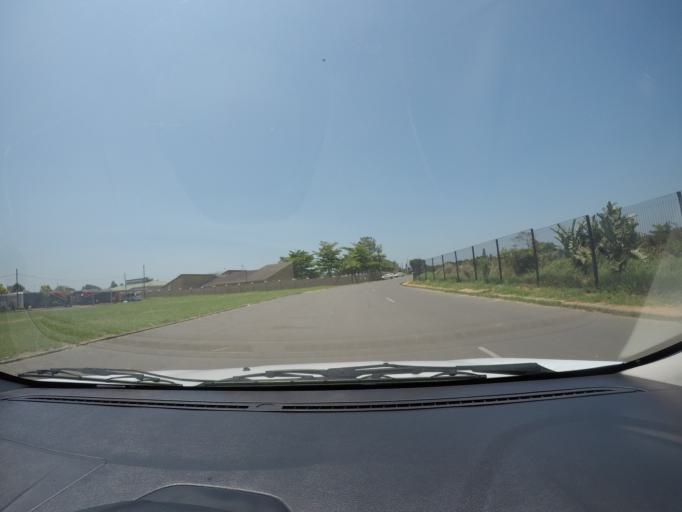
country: ZA
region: KwaZulu-Natal
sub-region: uThungulu District Municipality
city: eSikhawini
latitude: -28.8686
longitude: 31.9093
